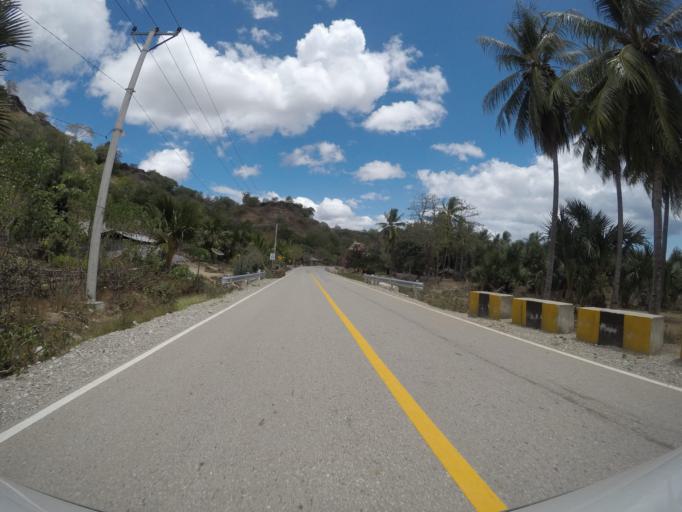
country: TL
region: Lautem
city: Lospalos
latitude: -8.4165
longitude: 126.7970
